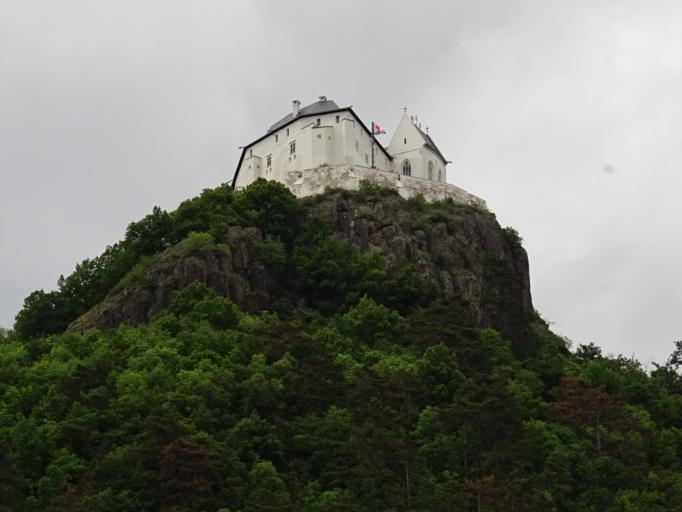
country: HU
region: Borsod-Abauj-Zemplen
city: Gonc
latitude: 48.5392
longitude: 21.4559
